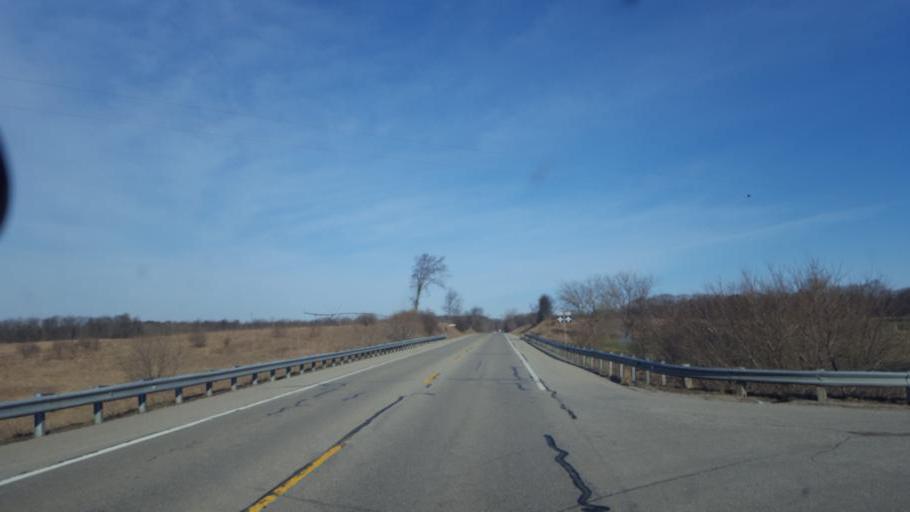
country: US
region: Michigan
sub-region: Montcalm County
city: Edmore
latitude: 43.4188
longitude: -85.1341
